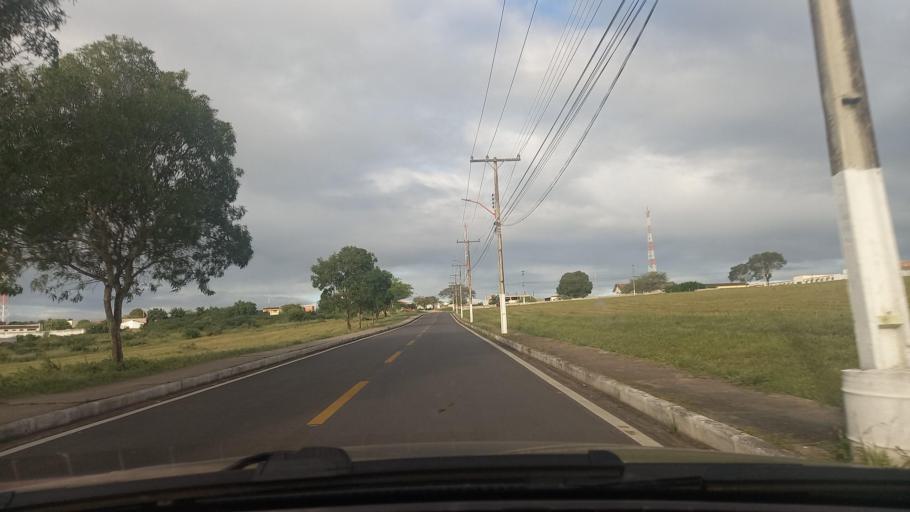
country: BR
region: Sergipe
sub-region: Caninde De Sao Francisco
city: Caninde de Sao Francisco
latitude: -9.6077
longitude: -37.7653
